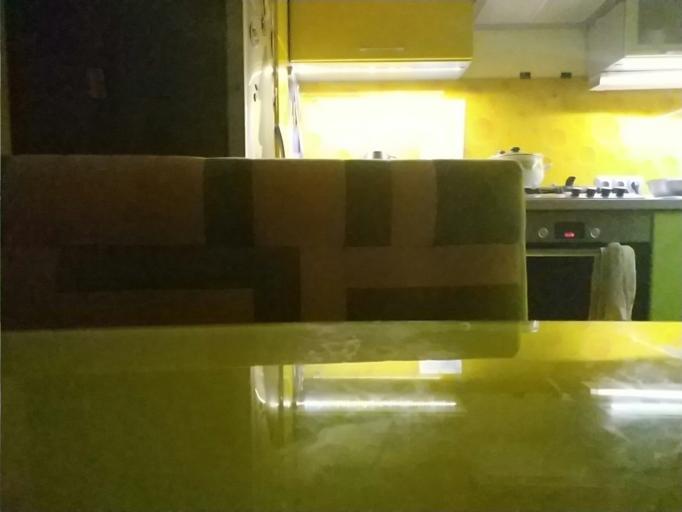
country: RU
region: Republic of Karelia
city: Kalevala
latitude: 65.3635
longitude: 30.6725
